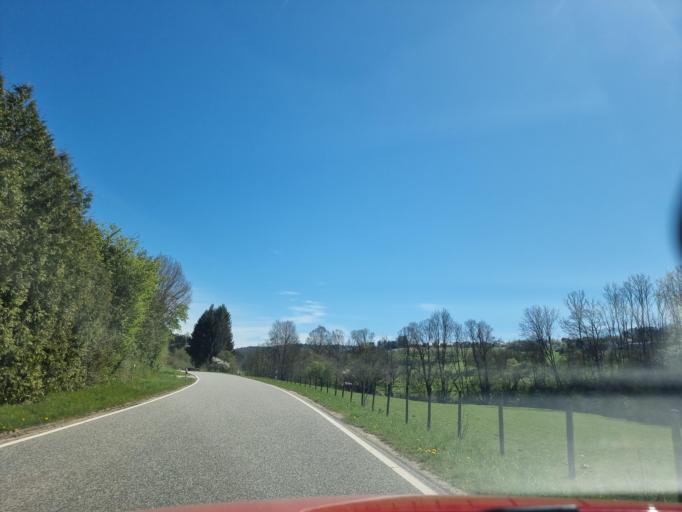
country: DE
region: Rheinland-Pfalz
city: Welschbillig
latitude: 49.8530
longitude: 6.5813
